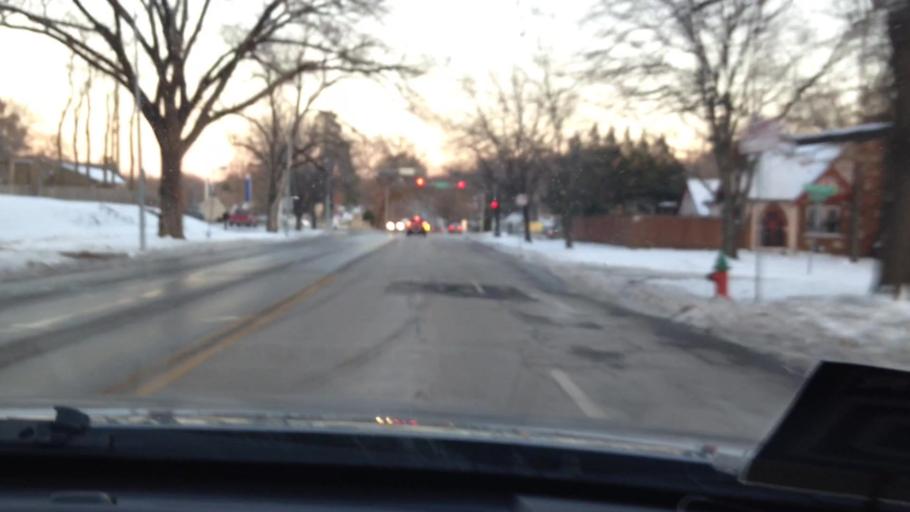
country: US
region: Kansas
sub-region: Johnson County
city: Mission Hills
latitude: 38.9989
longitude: -94.5767
